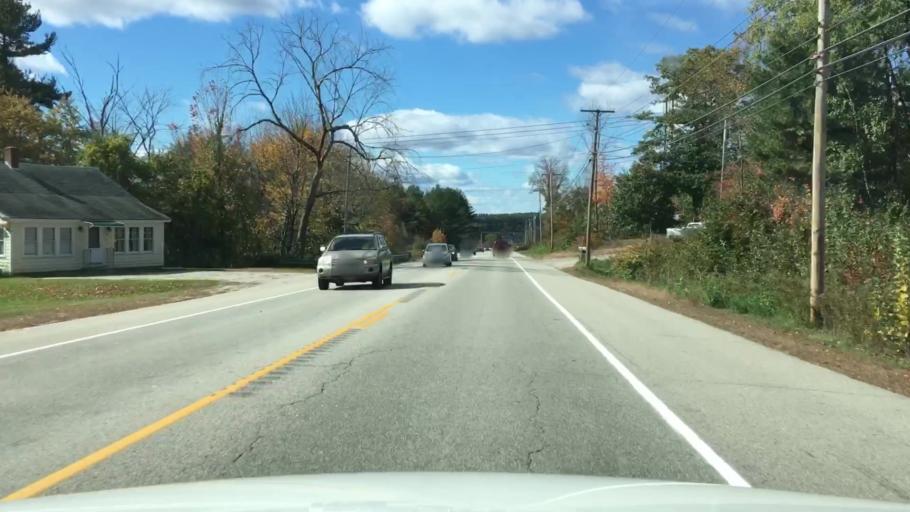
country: US
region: Maine
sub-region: York County
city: West Kennebunk
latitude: 43.4745
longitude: -70.5384
